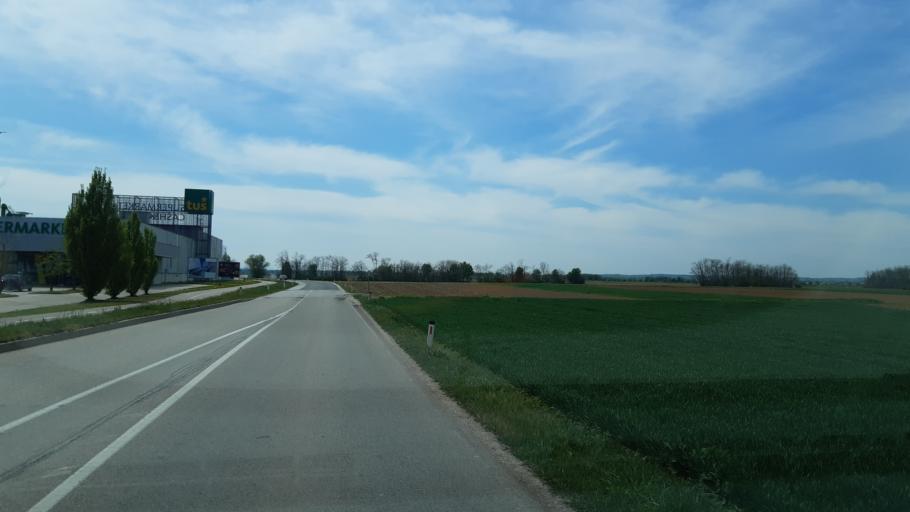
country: SI
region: Murska Sobota
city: Murska Sobota
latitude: 46.6457
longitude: 16.1674
